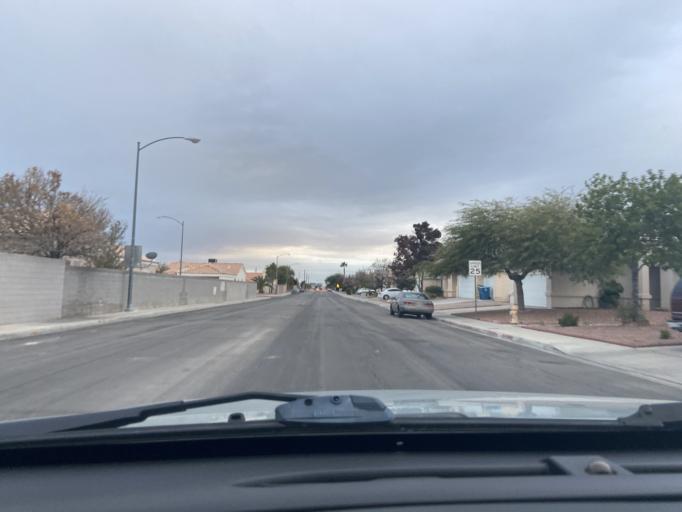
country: US
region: Nevada
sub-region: Clark County
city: Las Vegas
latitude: 36.2275
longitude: -115.1845
